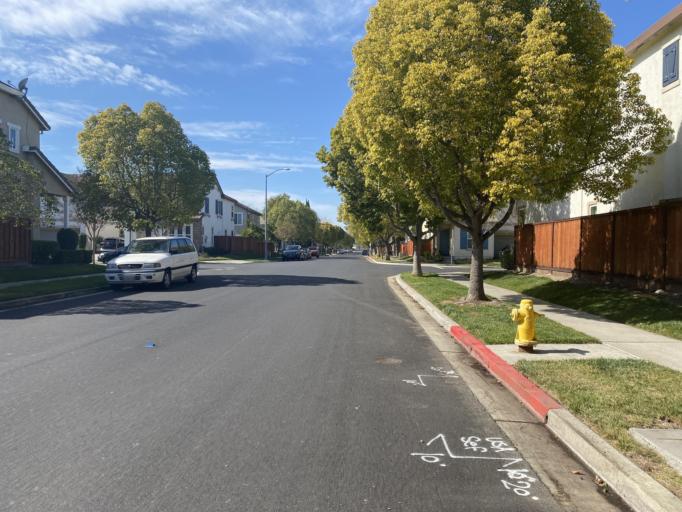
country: US
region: California
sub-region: Alameda County
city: Pleasanton
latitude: 37.6924
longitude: -121.8554
